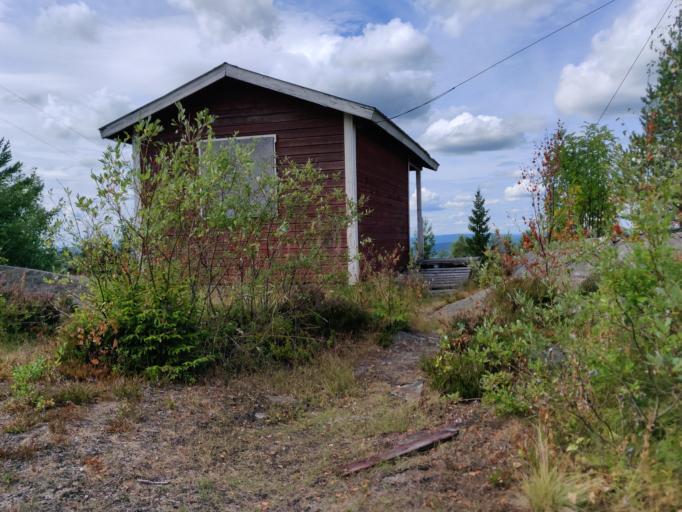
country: SE
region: Vaermland
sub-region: Hagfors Kommun
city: Hagfors
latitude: 60.0221
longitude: 13.7295
